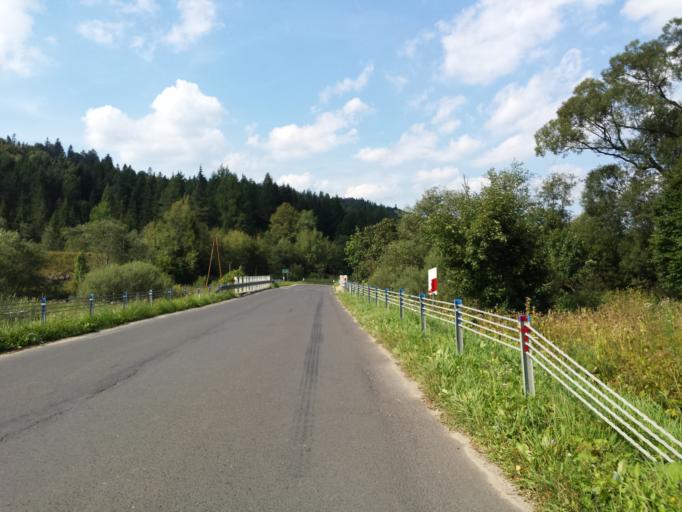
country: PL
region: Subcarpathian Voivodeship
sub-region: Powiat leski
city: Cisna
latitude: 49.2035
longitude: 22.3638
